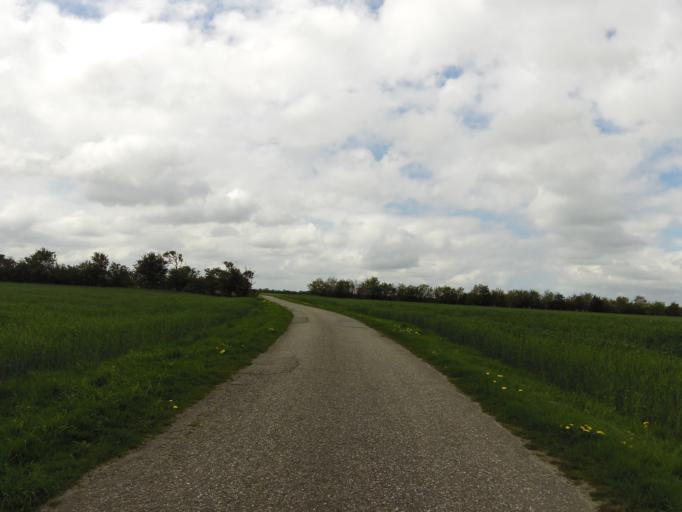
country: DK
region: South Denmark
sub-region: Haderslev Kommune
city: Gram
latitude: 55.2259
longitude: 8.9815
